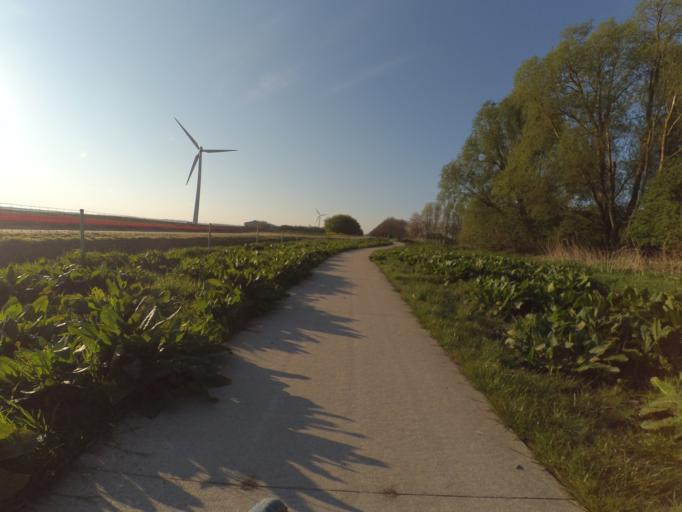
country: NL
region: Flevoland
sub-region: Gemeente Lelystad
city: Lelystad
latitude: 52.4329
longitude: 5.4348
